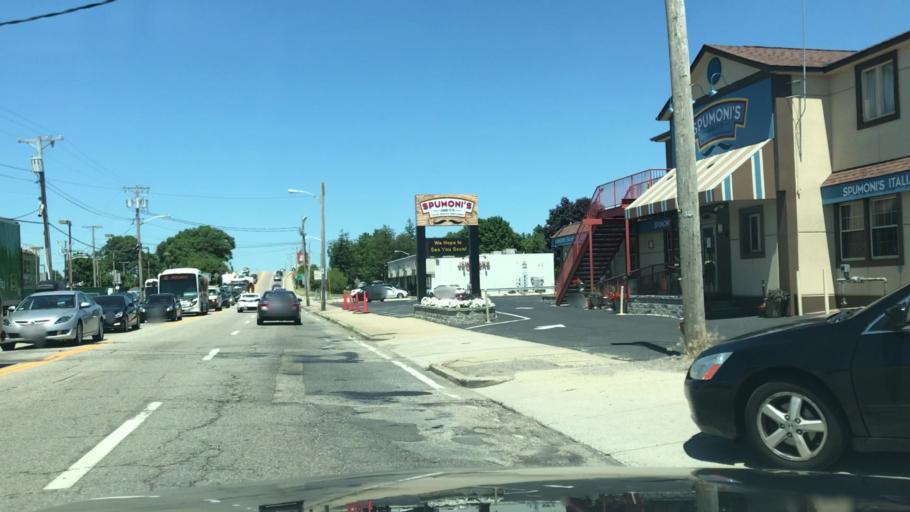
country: US
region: Massachusetts
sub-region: Bristol County
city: North Seekonk
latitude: 41.8946
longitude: -71.3541
